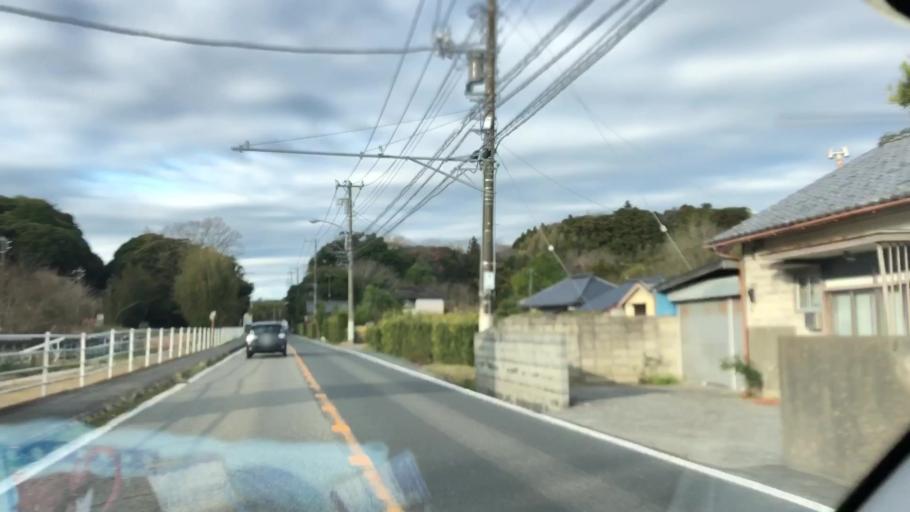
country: JP
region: Chiba
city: Tateyama
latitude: 34.9989
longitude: 139.8980
